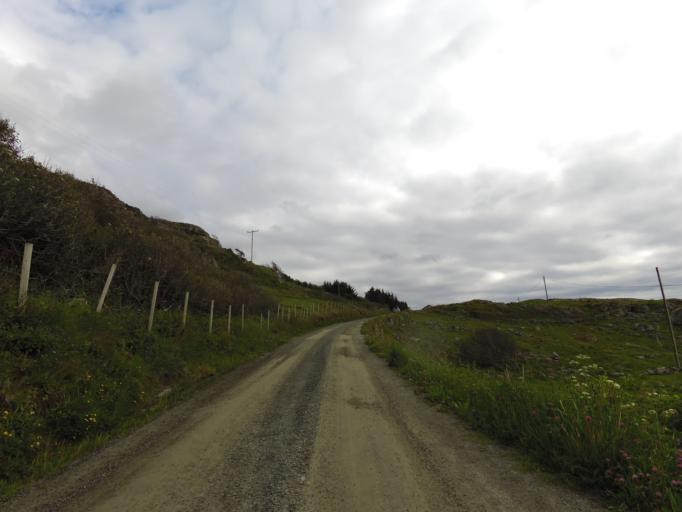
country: NO
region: Vest-Agder
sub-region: Farsund
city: Vestbygd
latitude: 58.1452
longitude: 6.6135
